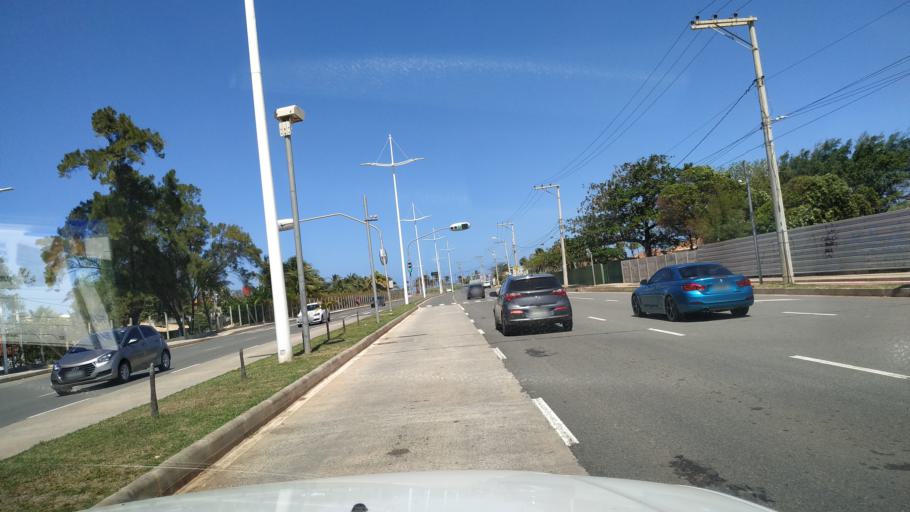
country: BR
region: Bahia
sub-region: Lauro De Freitas
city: Lauro de Freitas
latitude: -12.9511
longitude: -38.3849
